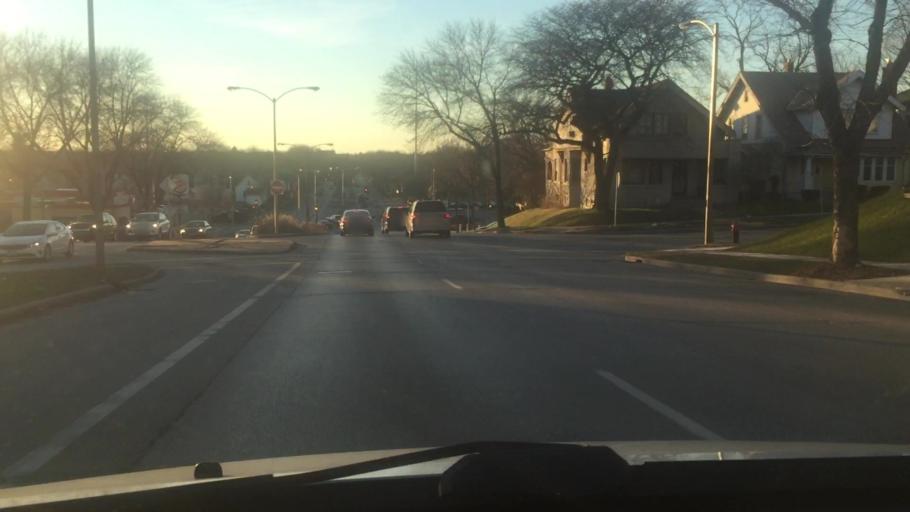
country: US
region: Wisconsin
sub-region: Milwaukee County
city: Shorewood
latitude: 43.0712
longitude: -87.9122
